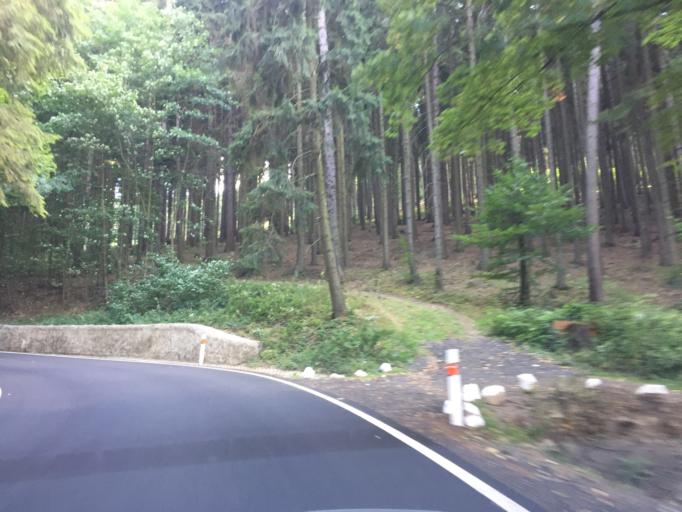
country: CZ
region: Liberecky
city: Mala Skala
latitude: 50.6362
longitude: 15.2068
